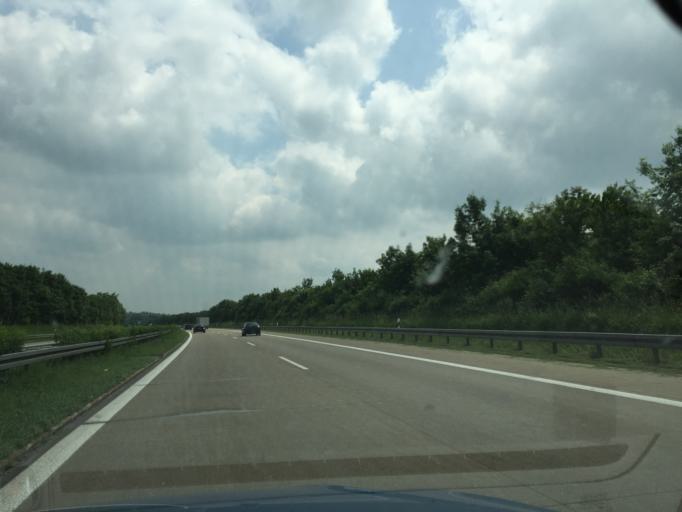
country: DE
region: Baden-Wuerttemberg
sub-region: Regierungsbezirk Stuttgart
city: Westhausen
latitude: 48.8380
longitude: 10.2015
